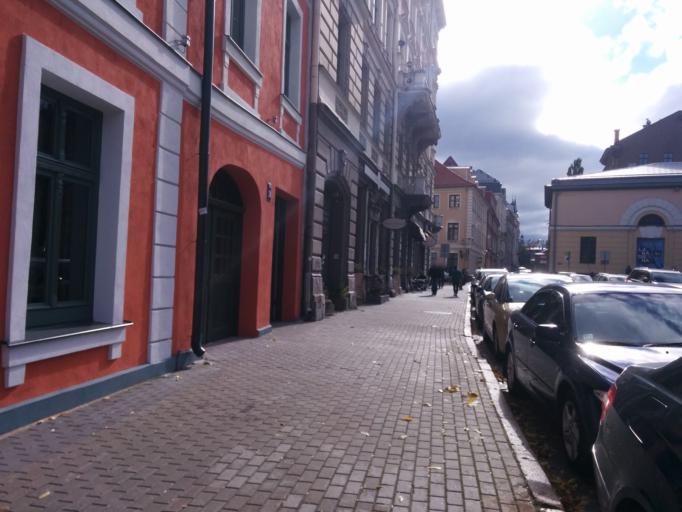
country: LV
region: Riga
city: Riga
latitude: 56.9522
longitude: 24.1052
